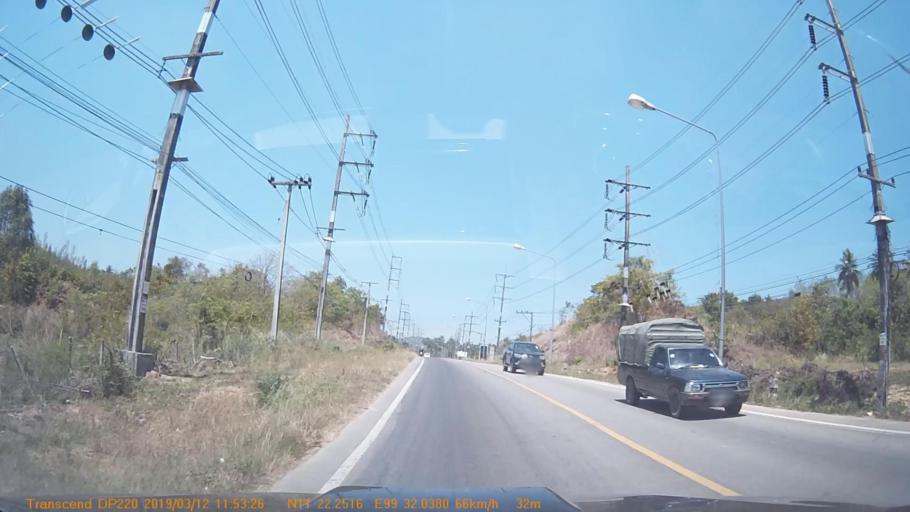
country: TH
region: Prachuap Khiri Khan
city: Thap Sakae
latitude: 11.3709
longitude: 99.5339
